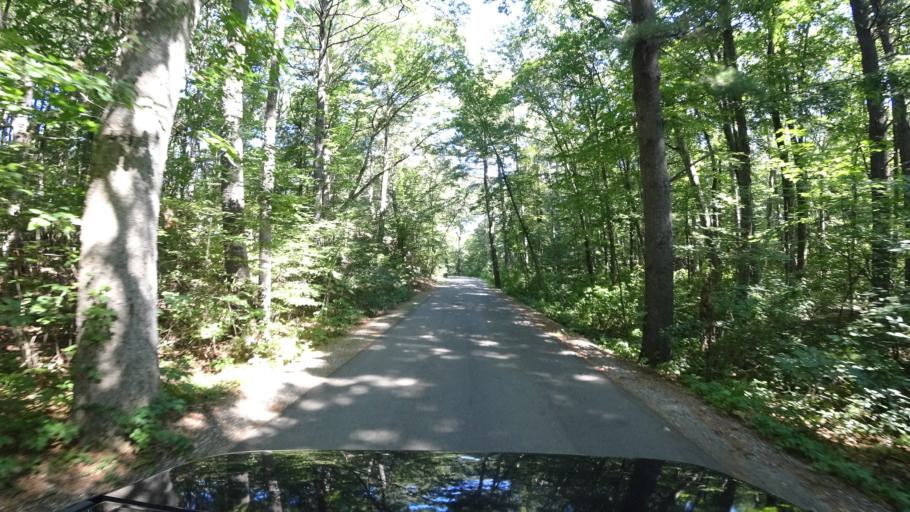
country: US
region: Massachusetts
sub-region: Norfolk County
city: Dedham
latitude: 42.2576
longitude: -71.1824
